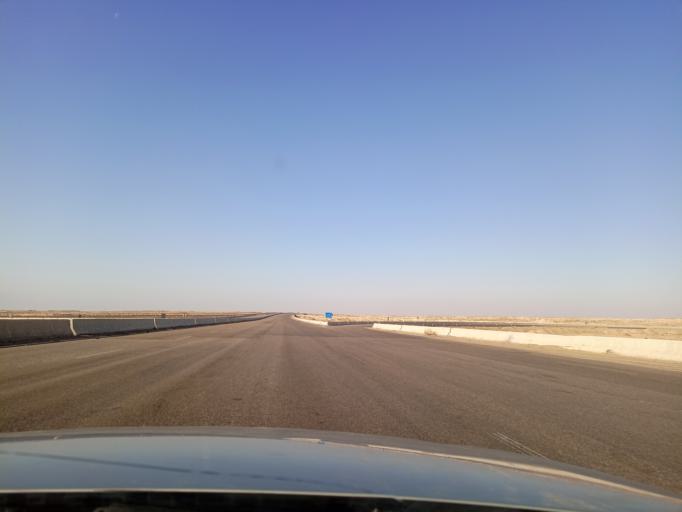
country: EG
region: Muhafazat al Fayyum
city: Tamiyah
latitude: 29.6250
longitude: 30.9569
